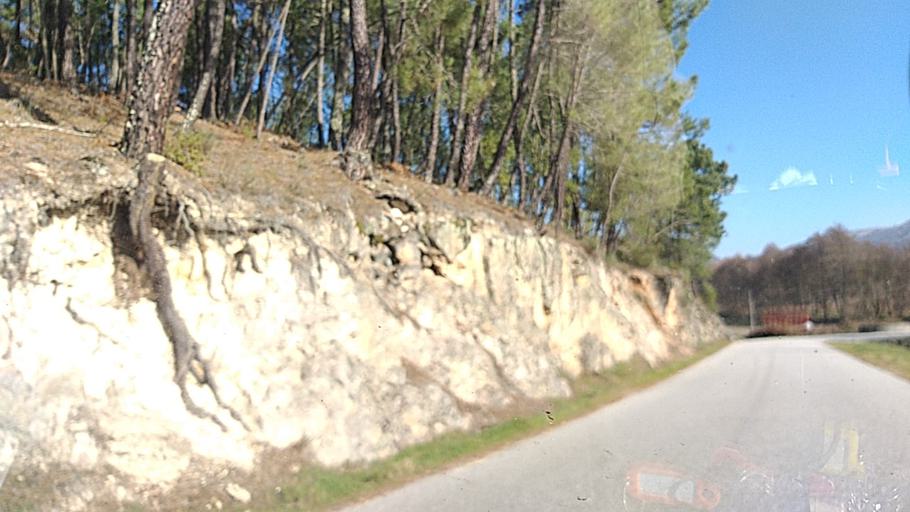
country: PT
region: Guarda
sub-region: Celorico da Beira
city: Celorico da Beira
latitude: 40.6961
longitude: -7.4517
